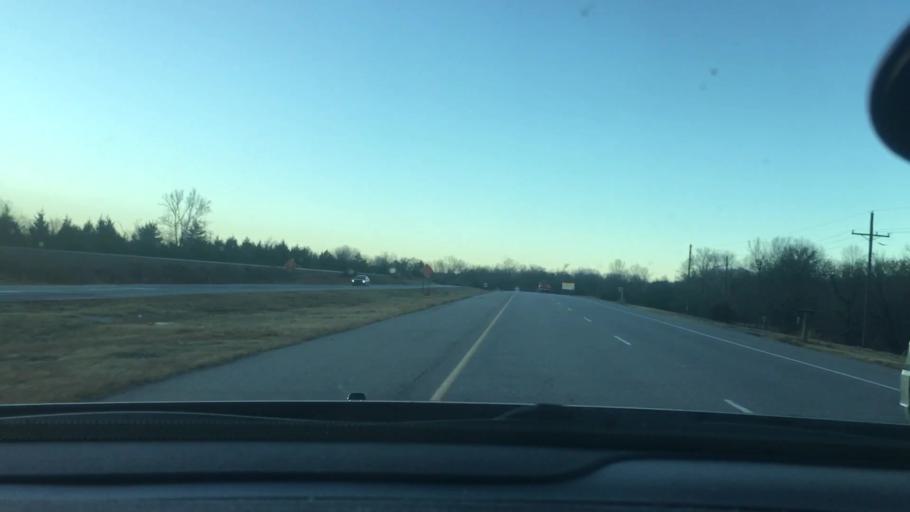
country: US
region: Oklahoma
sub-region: Pontotoc County
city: Ada
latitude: 34.7348
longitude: -96.7091
